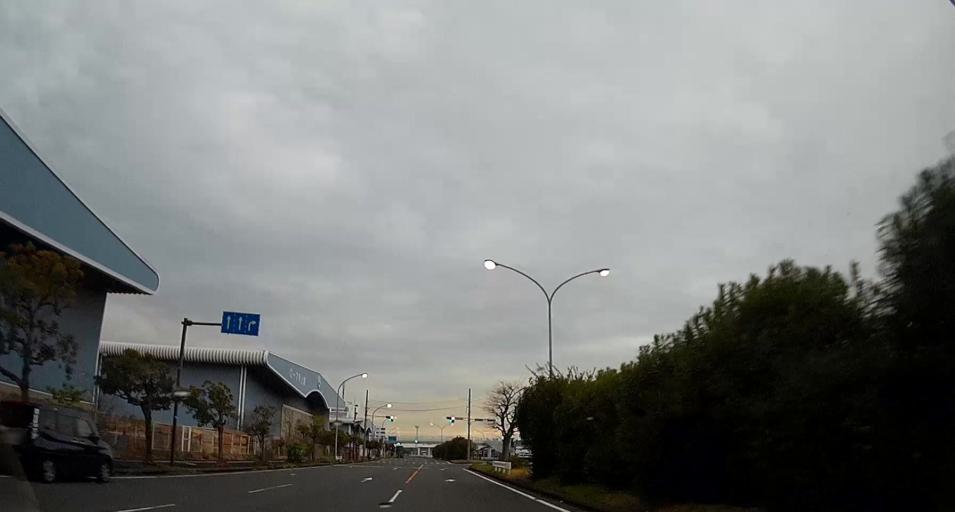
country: JP
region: Kanagawa
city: Yokohama
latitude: 35.4291
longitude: 139.6760
